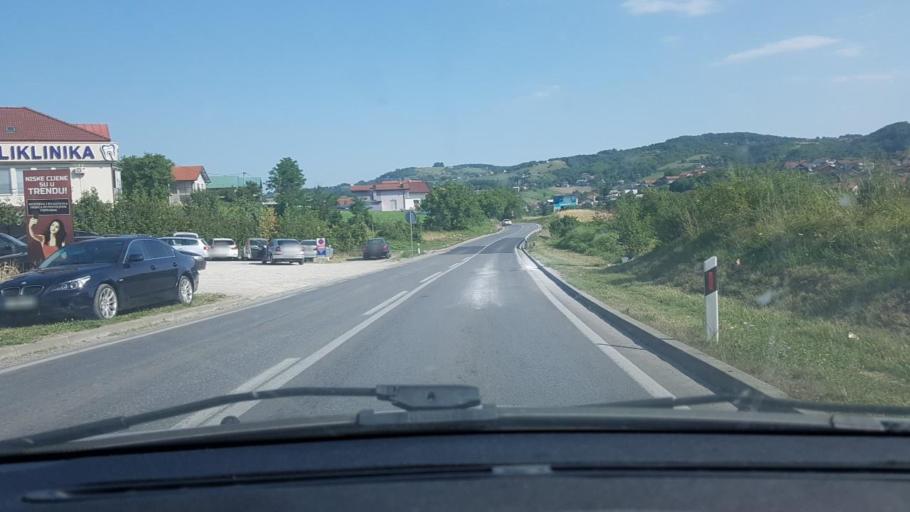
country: BA
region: Federation of Bosnia and Herzegovina
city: Cazin
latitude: 44.9615
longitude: 15.9277
